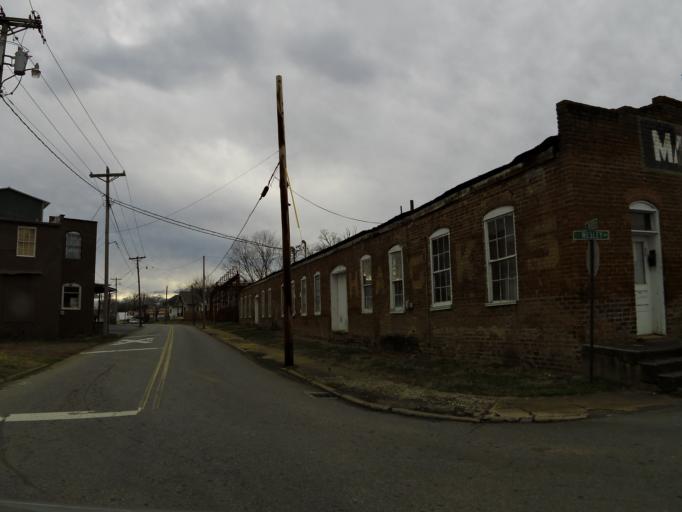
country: US
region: Tennessee
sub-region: Greene County
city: Greeneville
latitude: 36.1604
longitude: -82.8386
